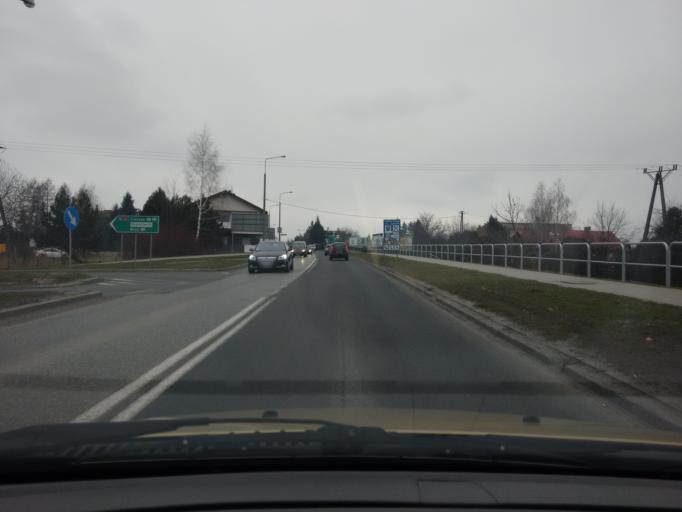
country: PL
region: Silesian Voivodeship
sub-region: Powiat cieszynski
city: Cieszyn
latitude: 49.7676
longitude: 18.6379
